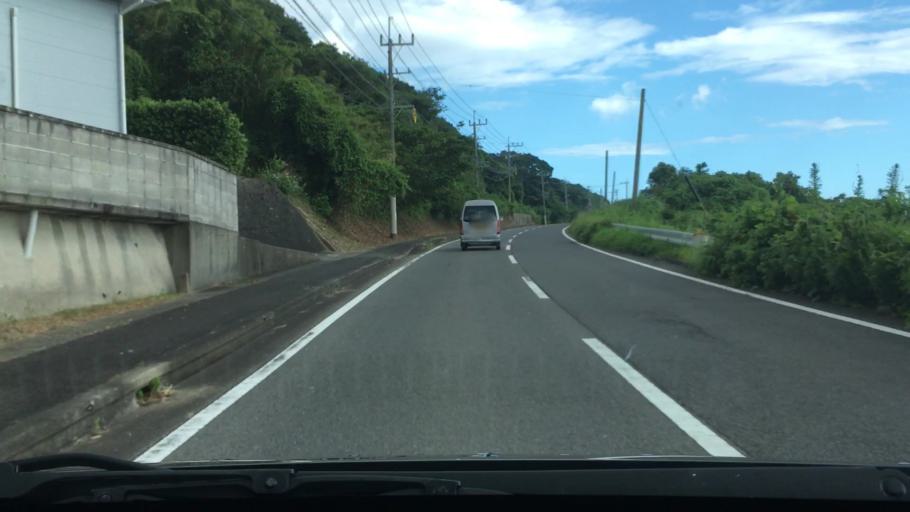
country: JP
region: Nagasaki
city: Togitsu
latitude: 32.8663
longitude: 129.6821
